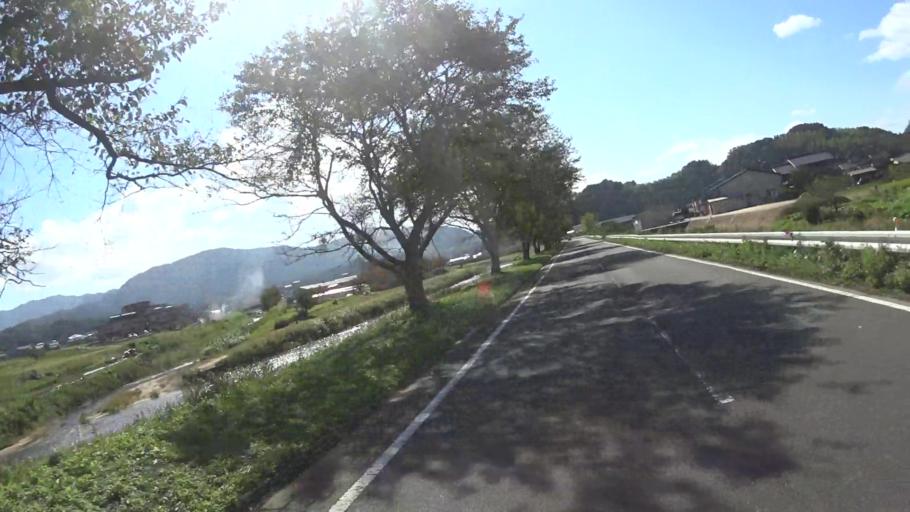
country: JP
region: Kyoto
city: Miyazu
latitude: 35.6631
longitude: 135.0864
